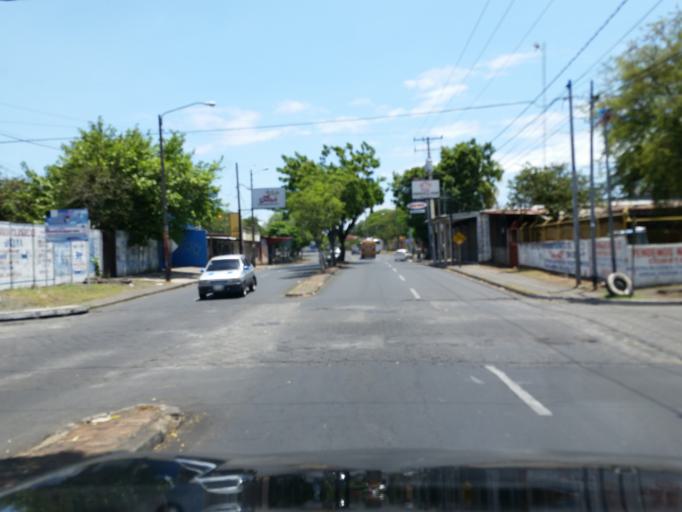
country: NI
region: Managua
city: Managua
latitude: 12.1464
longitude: -86.2455
